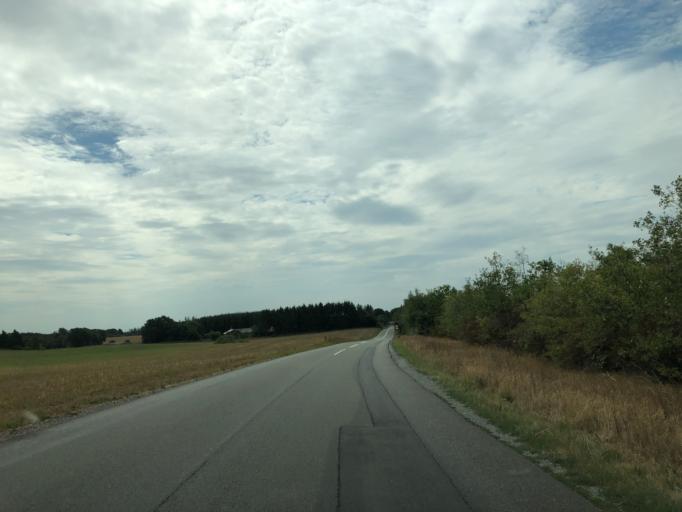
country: DK
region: South Denmark
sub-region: Vejle Kommune
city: Egtved
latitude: 55.6210
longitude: 9.1931
